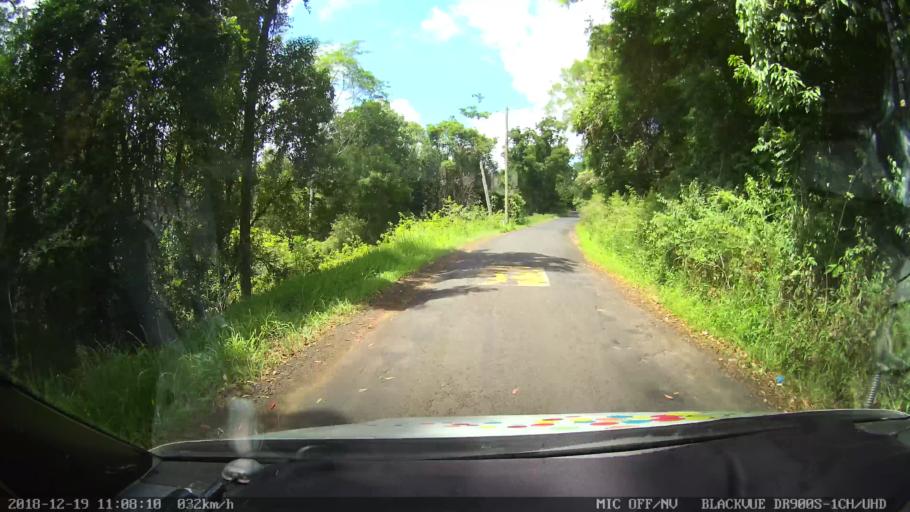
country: AU
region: New South Wales
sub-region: Lismore Municipality
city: Nimbin
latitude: -28.6296
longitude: 153.2667
